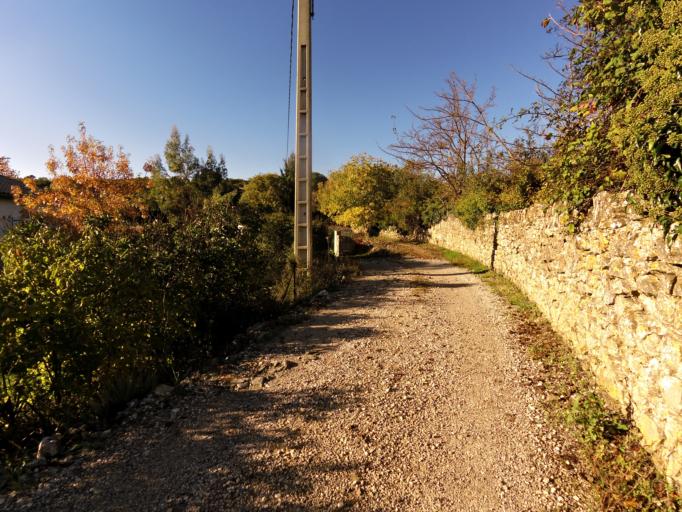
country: FR
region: Languedoc-Roussillon
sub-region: Departement du Gard
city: Sauve
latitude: 43.9917
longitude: 3.9525
